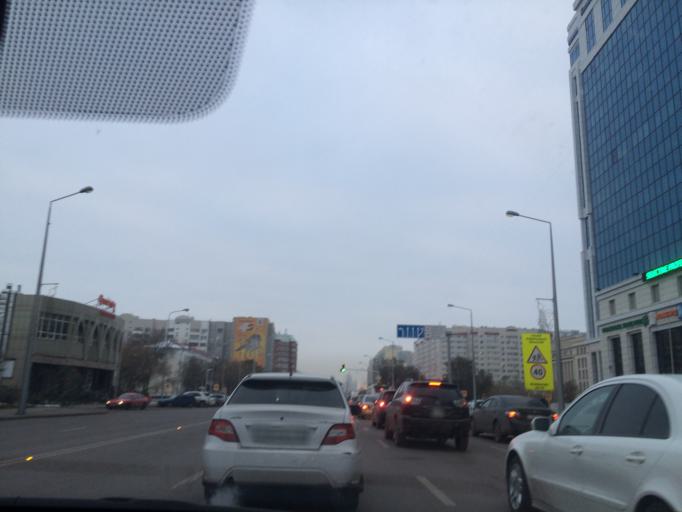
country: KZ
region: Astana Qalasy
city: Astana
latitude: 51.1673
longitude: 71.4085
